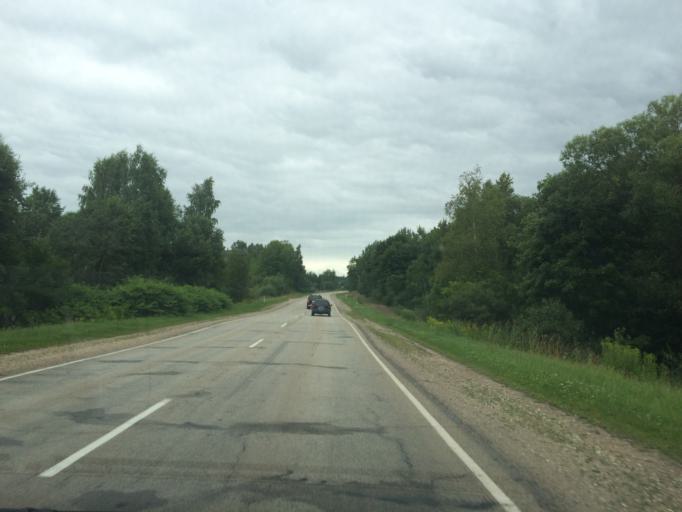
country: LV
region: Rezekne
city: Rezekne
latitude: 56.5648
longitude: 27.3667
